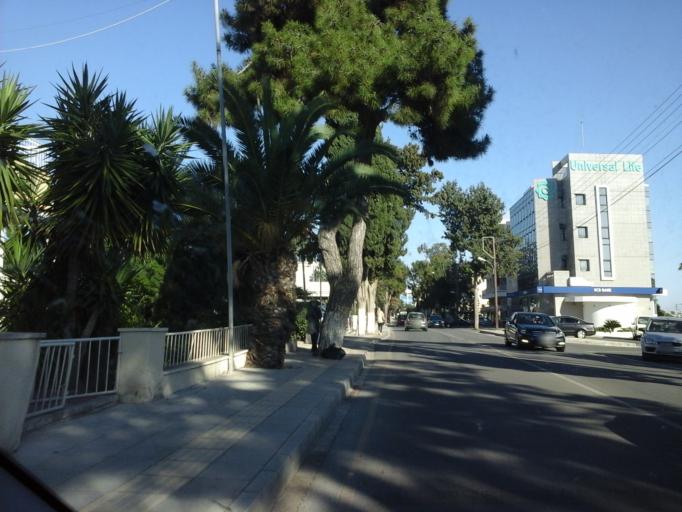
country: CY
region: Pafos
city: Paphos
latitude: 34.7724
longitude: 32.4268
